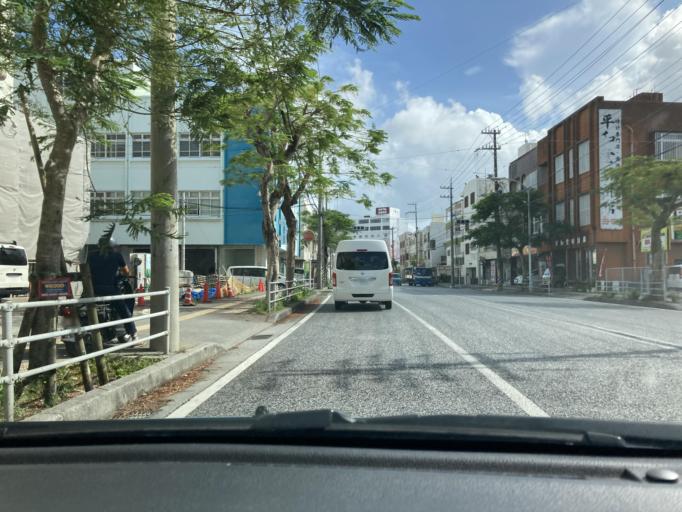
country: JP
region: Okinawa
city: Tomigusuku
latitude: 26.1983
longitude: 127.6758
